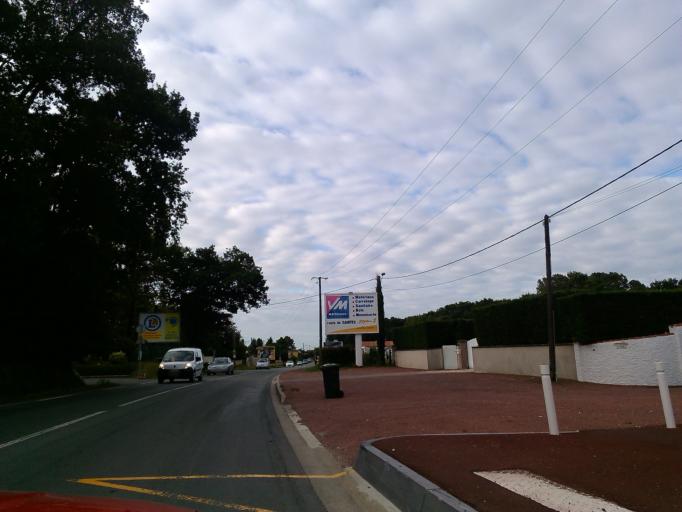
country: FR
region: Poitou-Charentes
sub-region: Departement de la Charente-Maritime
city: Royan
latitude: 45.6487
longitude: -1.0245
